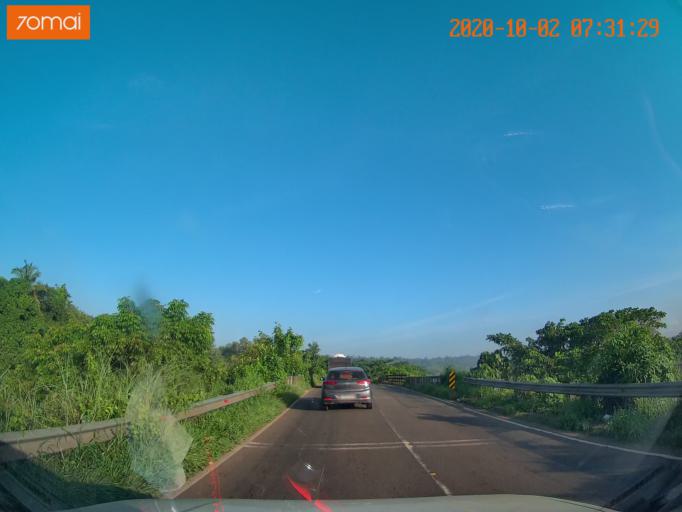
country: IN
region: Kerala
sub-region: Malappuram
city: Pariyapuram
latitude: 11.0489
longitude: 75.9385
